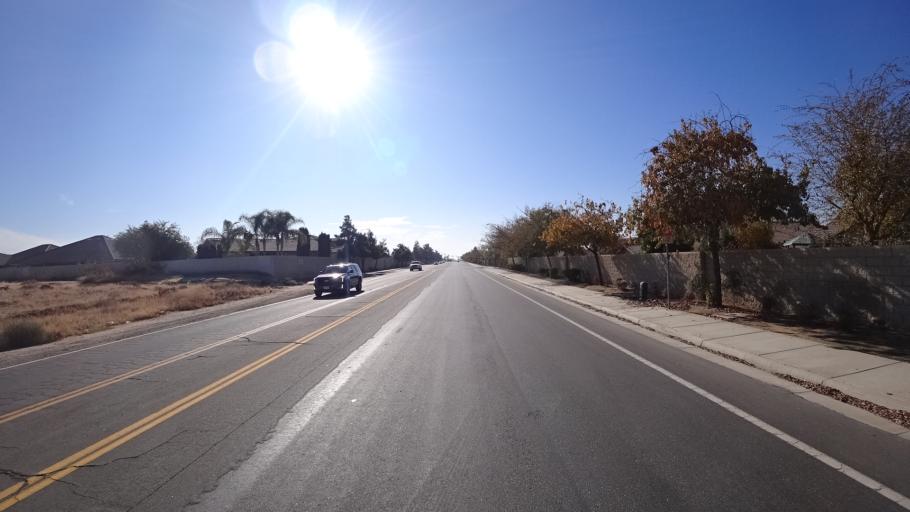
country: US
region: California
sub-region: Kern County
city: Rosedale
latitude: 35.4092
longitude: -119.1456
